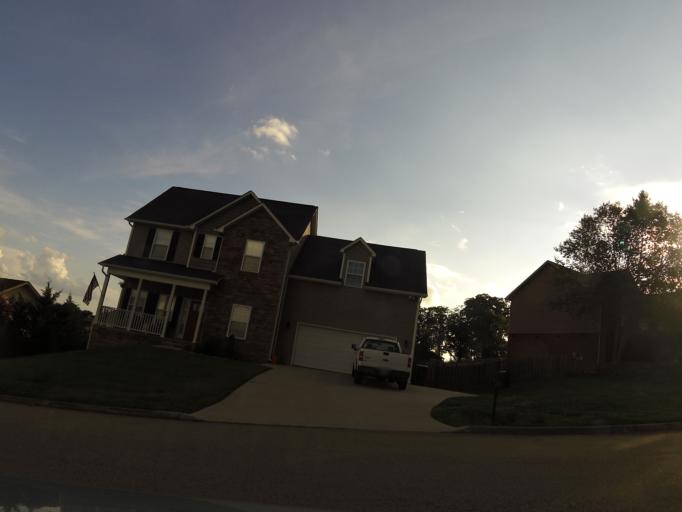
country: US
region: Tennessee
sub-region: Knox County
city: Knoxville
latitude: 36.0012
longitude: -84.0165
